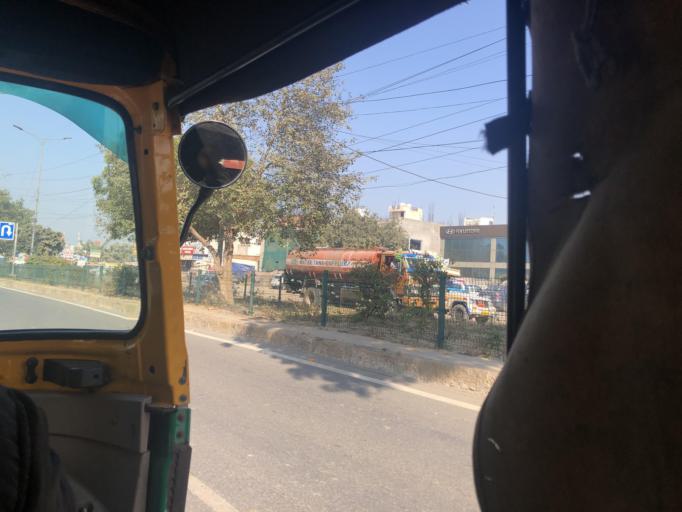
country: IN
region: Haryana
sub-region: Gurgaon
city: Gurgaon
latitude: 28.4385
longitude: 77.0894
